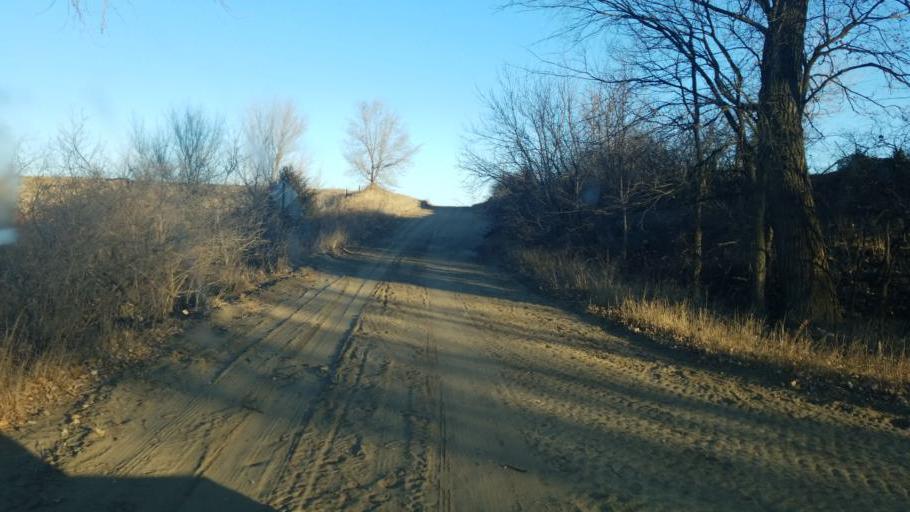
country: US
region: Nebraska
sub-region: Knox County
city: Center
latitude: 42.6117
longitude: -97.8378
